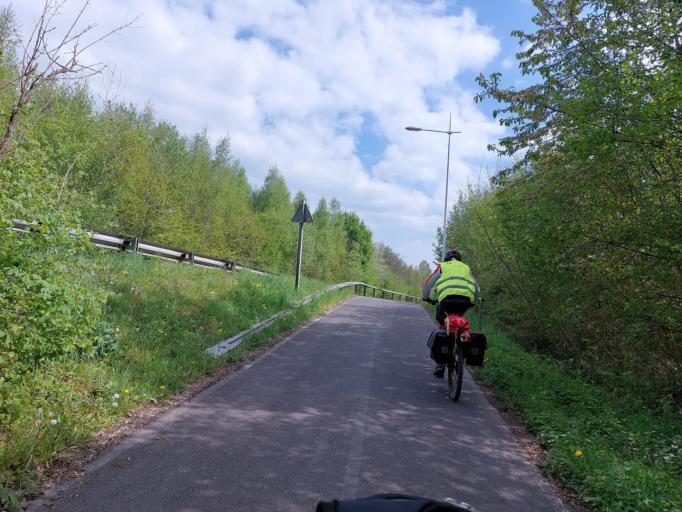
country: FR
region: Nord-Pas-de-Calais
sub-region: Departement du Nord
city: Hautmont
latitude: 50.2541
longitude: 3.8980
